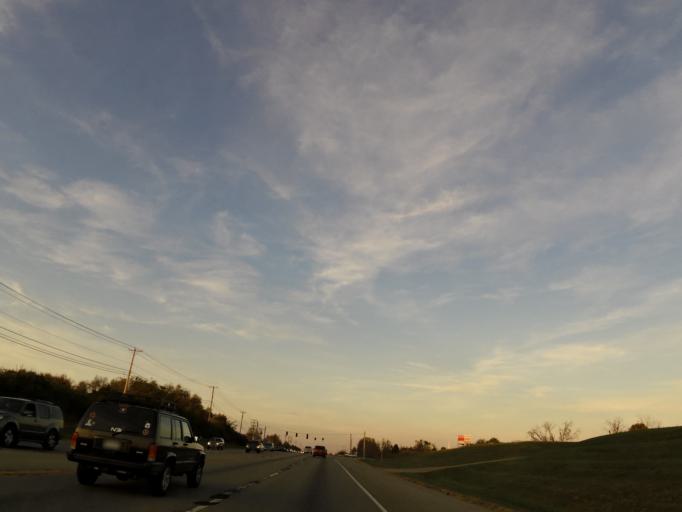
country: US
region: Kentucky
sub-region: Fayette County
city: Monticello
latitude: 37.9501
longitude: -84.5421
